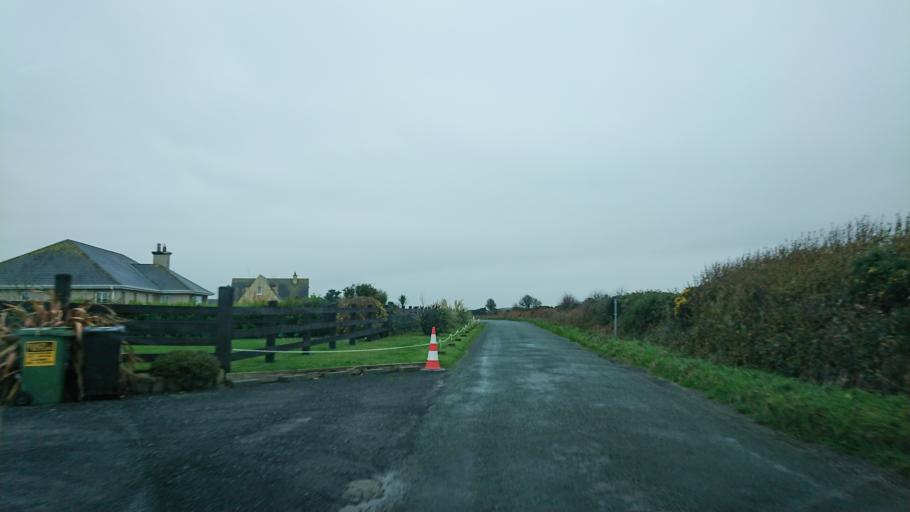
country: IE
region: Munster
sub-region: Waterford
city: Dunmore East
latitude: 52.1543
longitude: -7.0581
